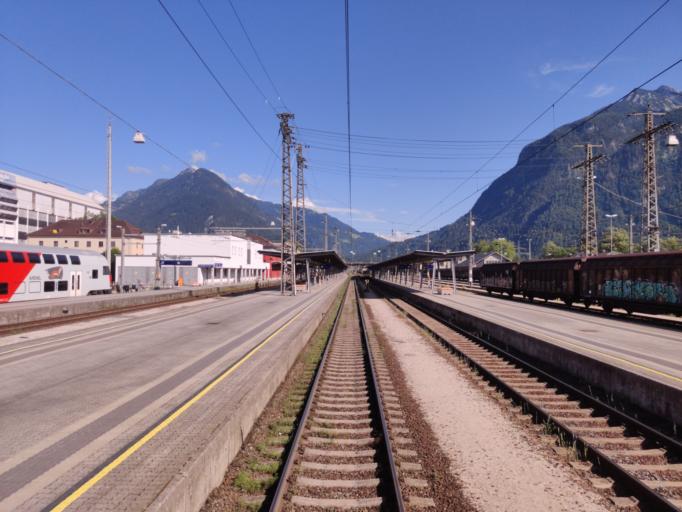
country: AT
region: Vorarlberg
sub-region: Politischer Bezirk Bludenz
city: Bludenz
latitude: 47.1562
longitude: 9.8129
